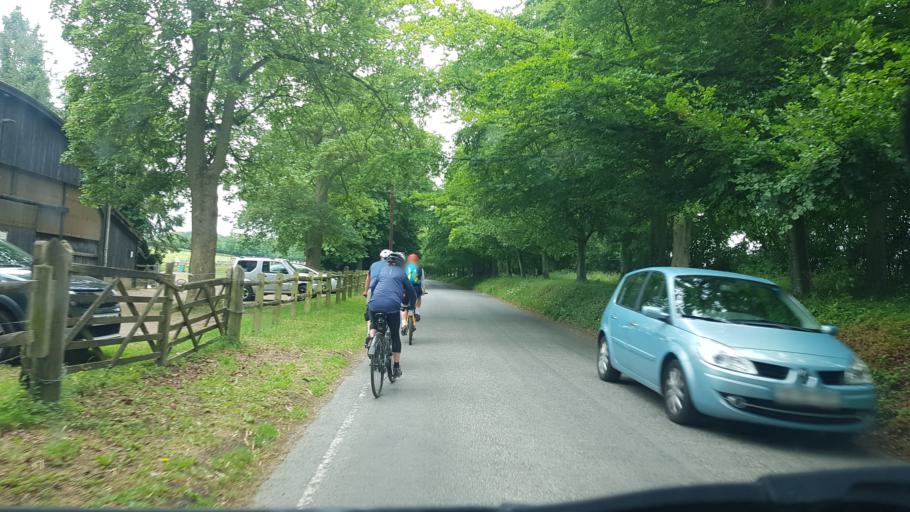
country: GB
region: England
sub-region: Surrey
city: Great Bookham
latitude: 51.2713
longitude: -0.3671
